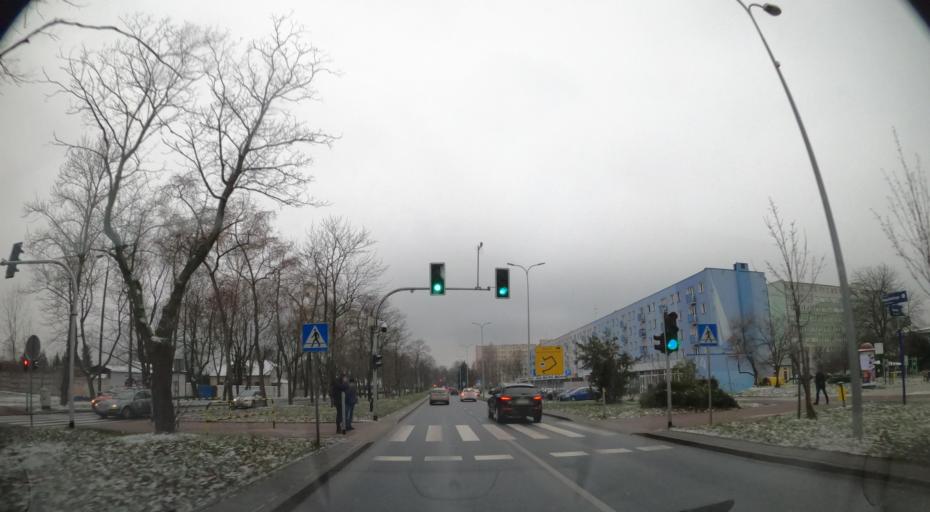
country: PL
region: Masovian Voivodeship
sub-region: Plock
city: Plock
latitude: 52.5504
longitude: 19.6870
